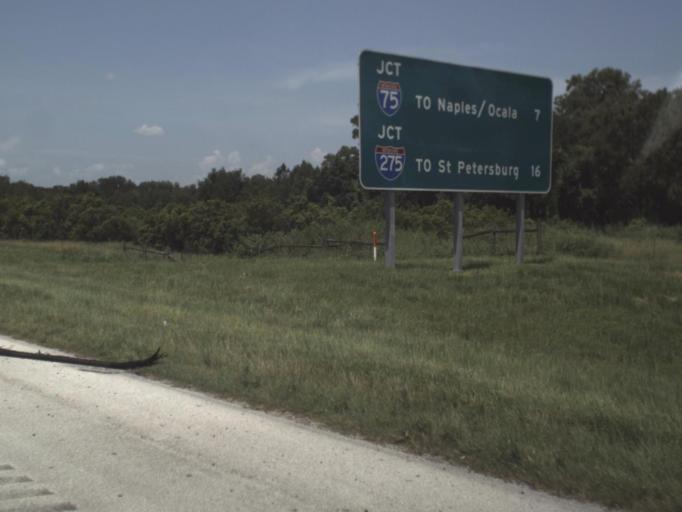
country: US
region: Florida
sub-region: Hillsborough County
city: Dover
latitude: 28.0278
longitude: -82.2065
